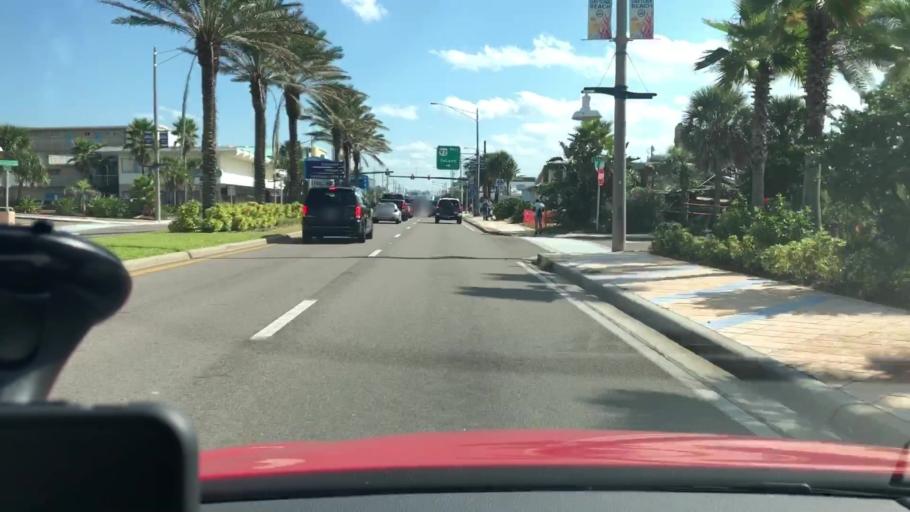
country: US
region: Florida
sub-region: Volusia County
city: Daytona Beach
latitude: 29.2231
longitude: -81.0065
